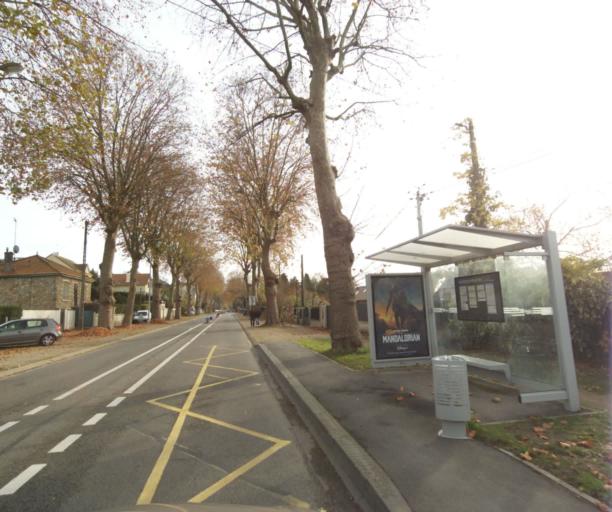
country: FR
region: Ile-de-France
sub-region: Departement des Yvelines
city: Triel-sur-Seine
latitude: 48.9907
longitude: 1.9912
